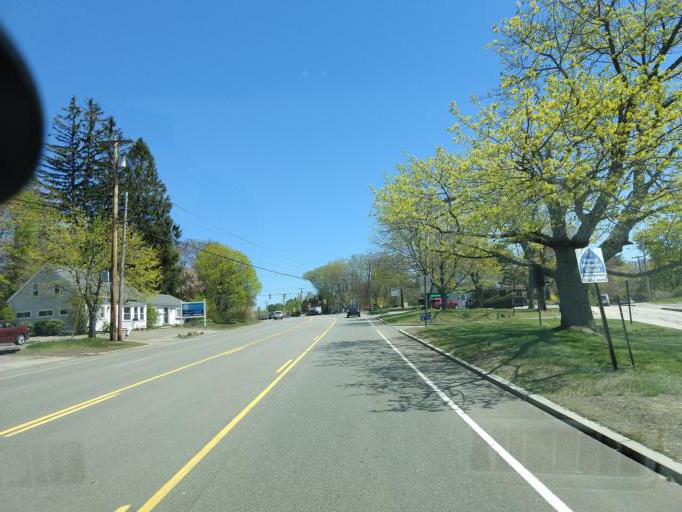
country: US
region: Maine
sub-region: York County
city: York Harbor
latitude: 43.1507
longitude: -70.6654
